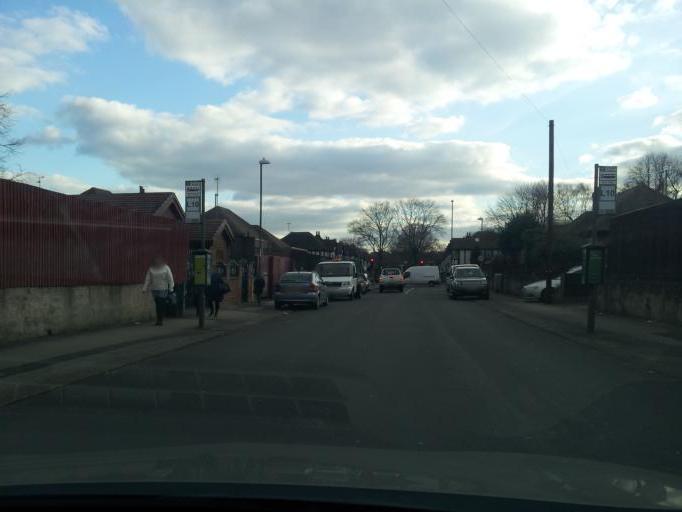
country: GB
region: England
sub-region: Nottingham
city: Nottingham
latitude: 52.9555
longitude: -1.1990
